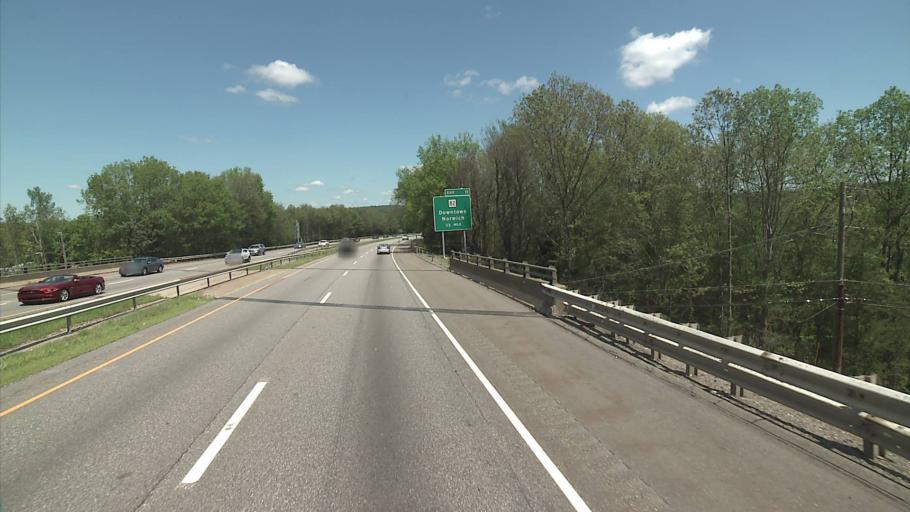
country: US
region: Connecticut
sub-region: New London County
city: Montville Center
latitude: 41.4980
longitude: -72.1155
